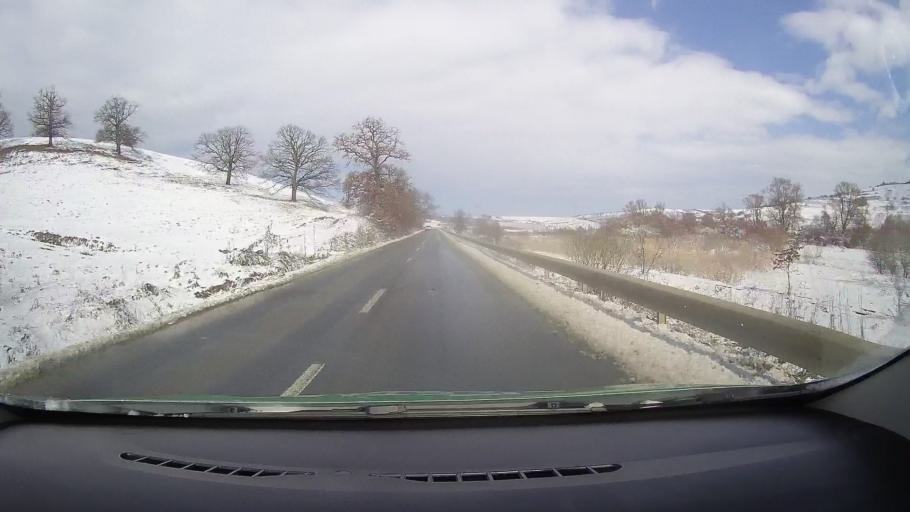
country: RO
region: Sibiu
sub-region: Comuna Altina
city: Altina
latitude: 45.9524
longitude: 24.4528
